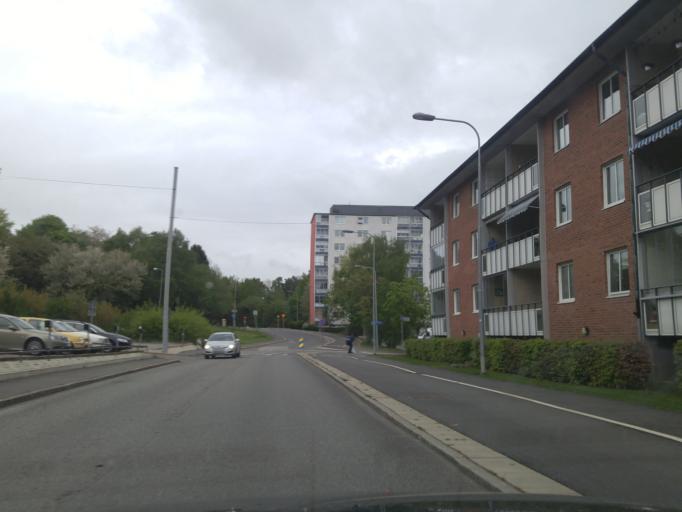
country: SE
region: Vaestra Goetaland
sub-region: Goteborg
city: Majorna
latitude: 57.6716
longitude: 11.9315
